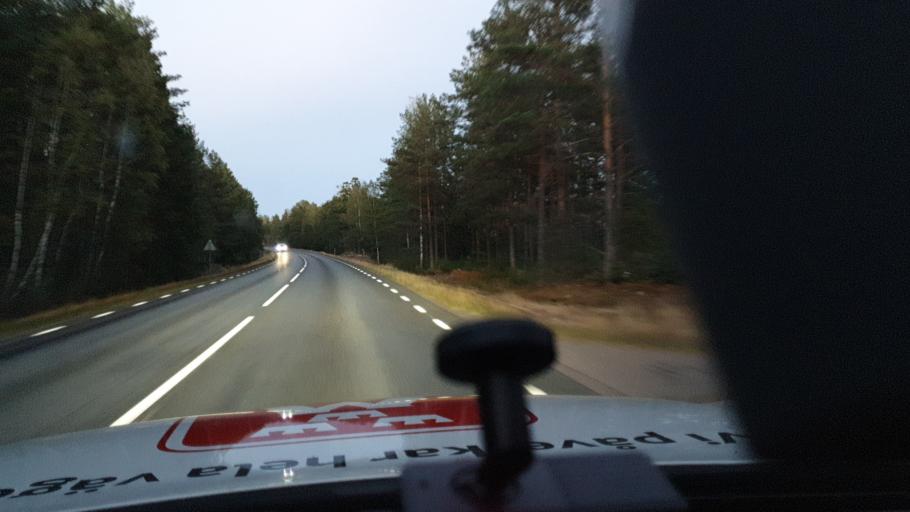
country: SE
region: Kalmar
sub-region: Oskarshamns Kommun
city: Paskallavik
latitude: 57.1865
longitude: 16.4115
